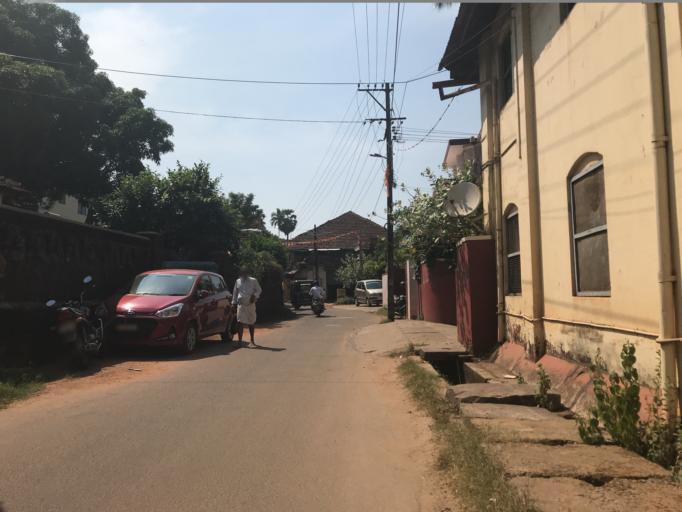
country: IN
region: Karnataka
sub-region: Dakshina Kannada
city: Mangalore
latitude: 12.8664
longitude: 74.8367
